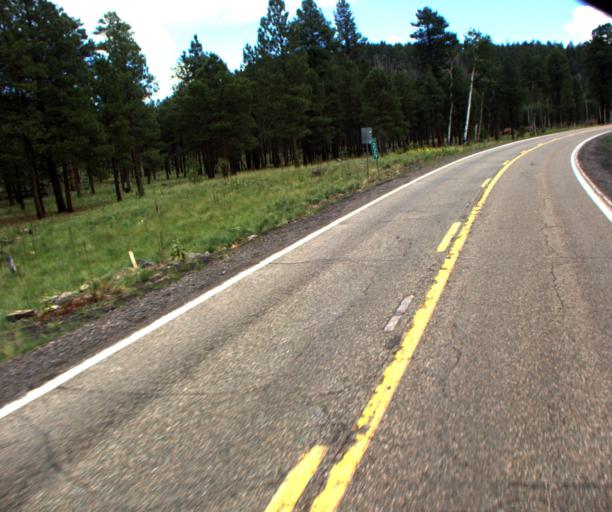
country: US
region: Arizona
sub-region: Coconino County
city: Flagstaff
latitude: 35.3263
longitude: -111.7740
